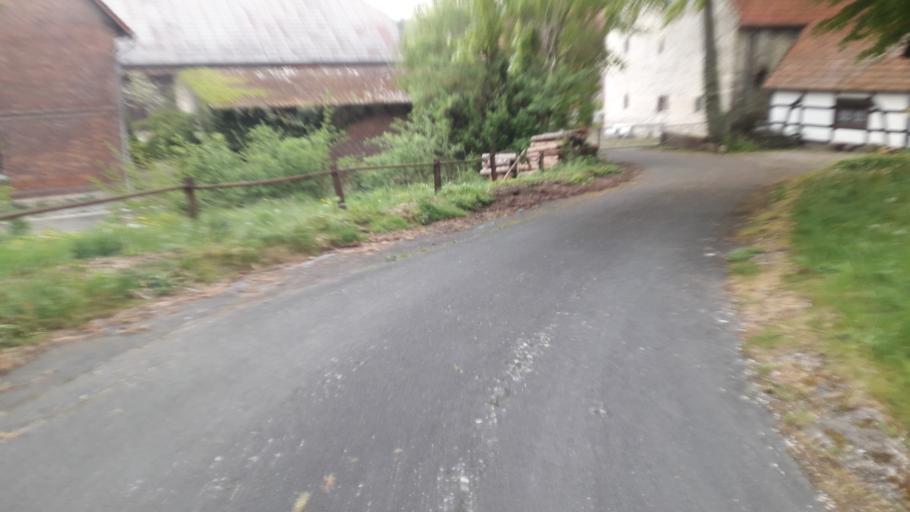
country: DE
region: North Rhine-Westphalia
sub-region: Regierungsbezirk Detmold
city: Paderborn
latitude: 51.6599
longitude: 8.7355
